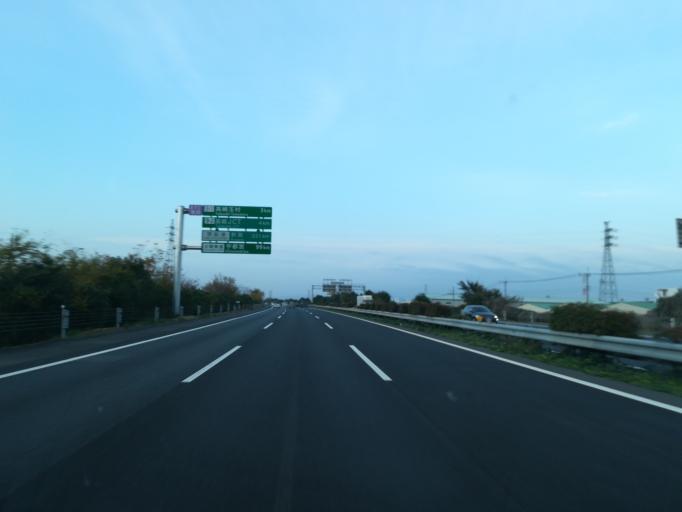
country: JP
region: Gunma
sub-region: Sawa-gun
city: Tamamura
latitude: 36.2903
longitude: 139.0980
